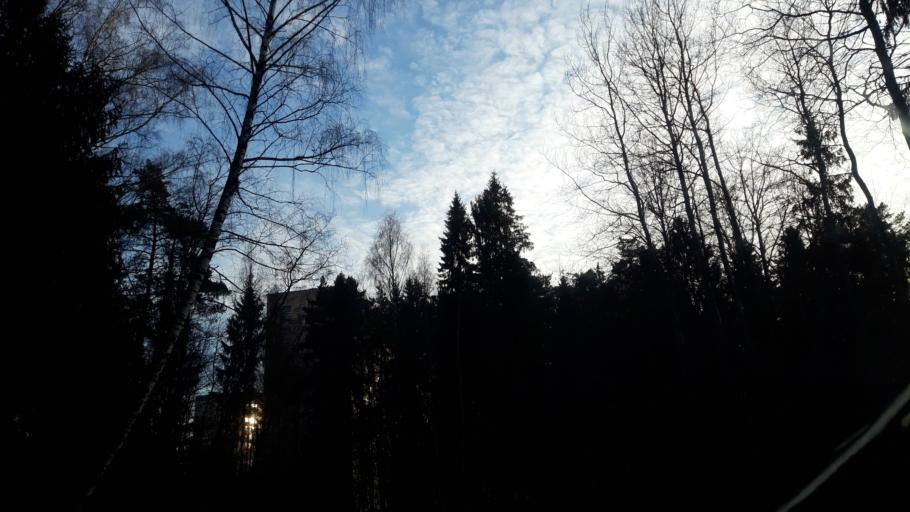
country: RU
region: Moskovskaya
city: Rzhavki
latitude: 56.0001
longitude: 37.2281
